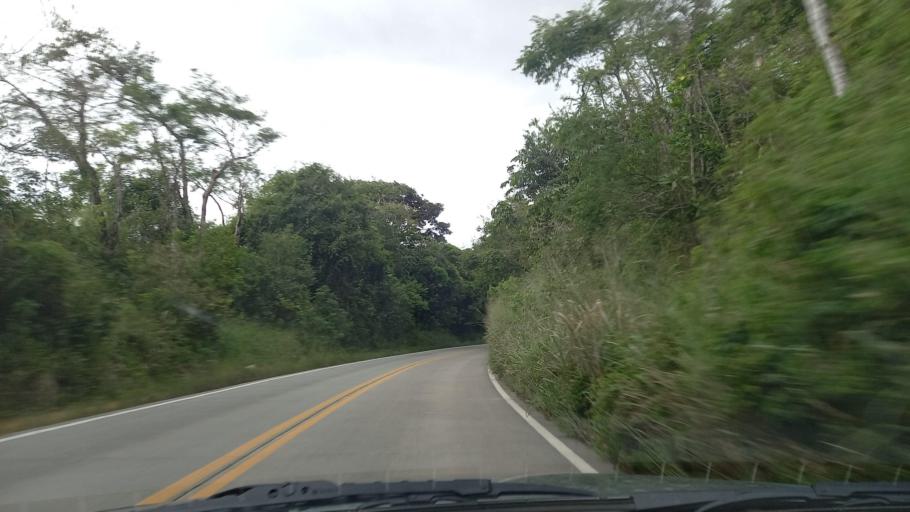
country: BR
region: Pernambuco
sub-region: Quipapa
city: Quipapa
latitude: -8.7898
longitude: -35.9927
